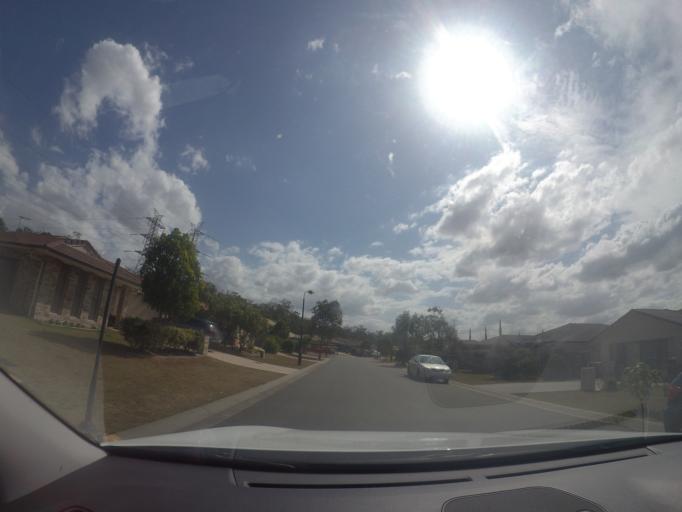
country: AU
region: Queensland
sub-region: Logan
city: Woodridge
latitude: -27.6606
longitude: 153.0772
